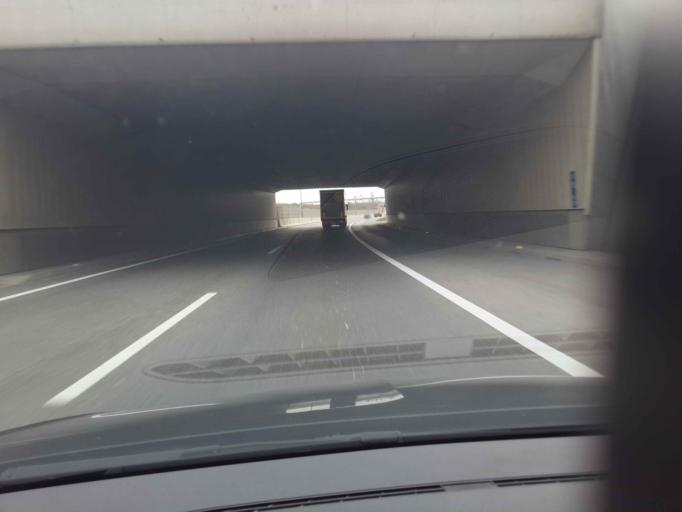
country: AT
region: Lower Austria
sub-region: Politischer Bezirk Wien-Umgebung
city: Schwechat
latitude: 48.1295
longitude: 16.4881
